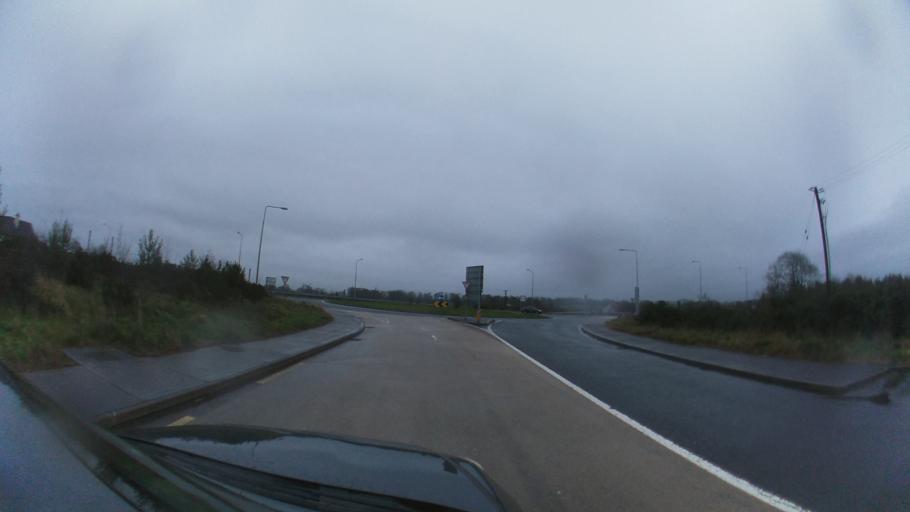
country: IE
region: Leinster
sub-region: County Carlow
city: Bagenalstown
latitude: 52.6739
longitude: -7.0268
